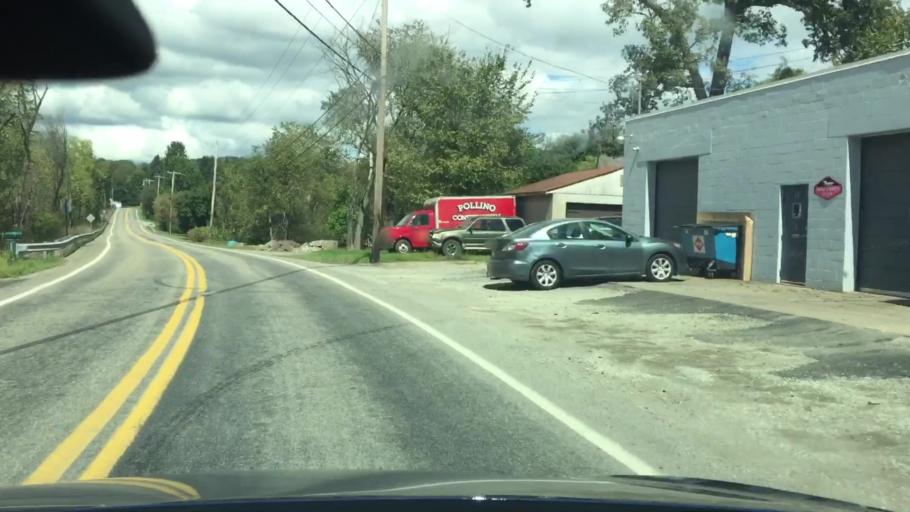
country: US
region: Pennsylvania
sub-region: Allegheny County
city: Russellton
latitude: 40.6242
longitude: -79.8324
